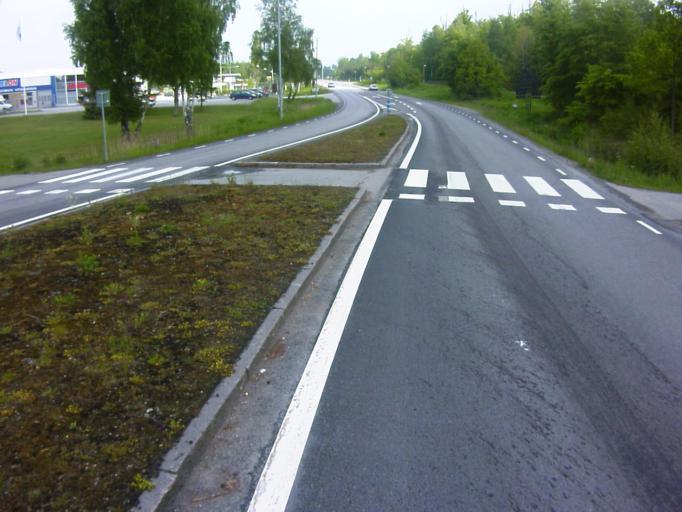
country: SE
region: Blekinge
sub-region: Solvesborgs Kommun
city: Soelvesborg
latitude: 56.0546
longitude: 14.5684
